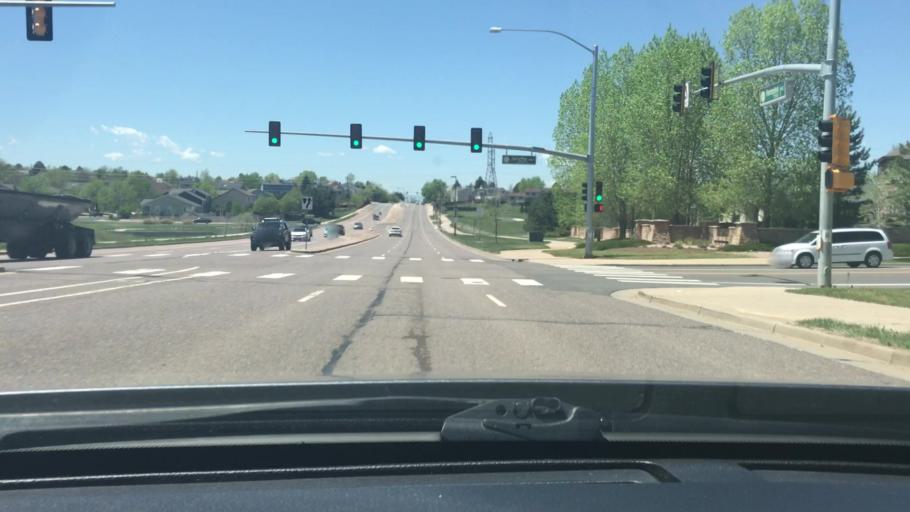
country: US
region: Colorado
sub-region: Arapahoe County
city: Dove Valley
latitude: 39.6531
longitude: -104.7500
